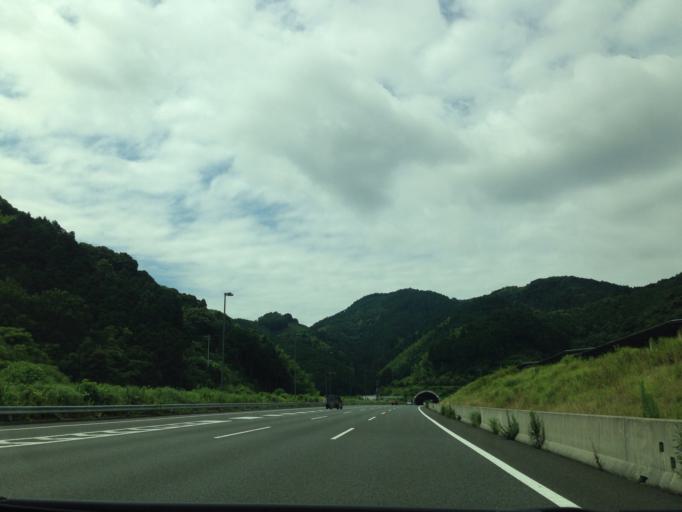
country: JP
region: Shizuoka
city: Shizuoka-shi
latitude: 34.9676
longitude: 138.2918
